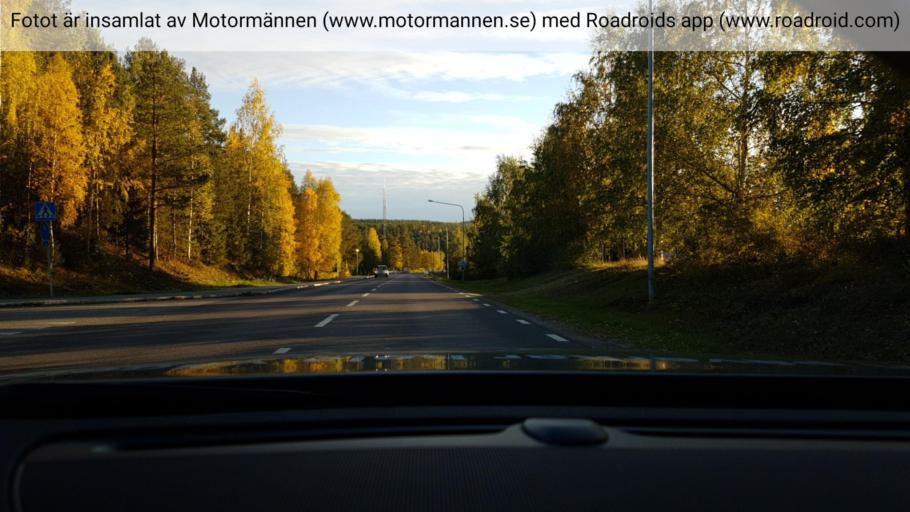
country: SE
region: Norrbotten
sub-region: Jokkmokks Kommun
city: Jokkmokk
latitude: 66.6060
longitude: 19.8226
